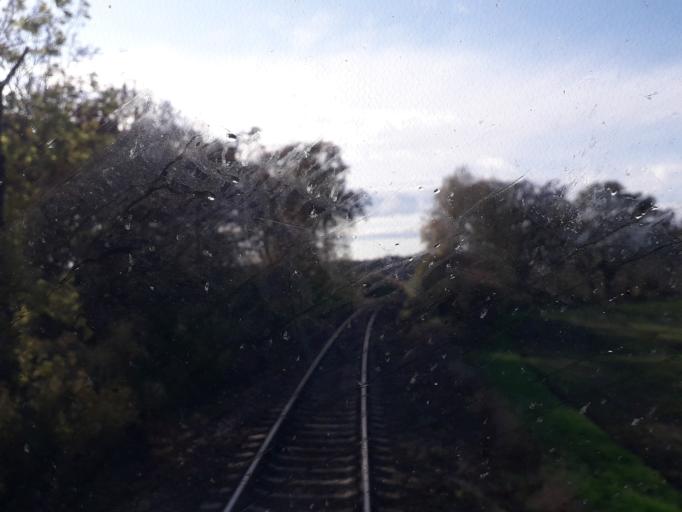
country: DE
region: Brandenburg
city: Gross Pankow
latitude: 53.1296
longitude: 12.0878
